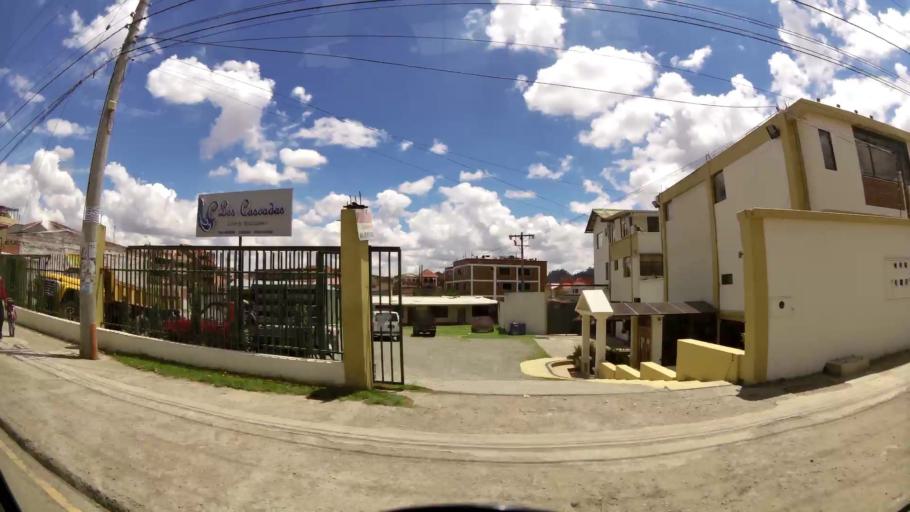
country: EC
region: Azuay
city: Cuenca
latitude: -2.9184
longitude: -79.0389
